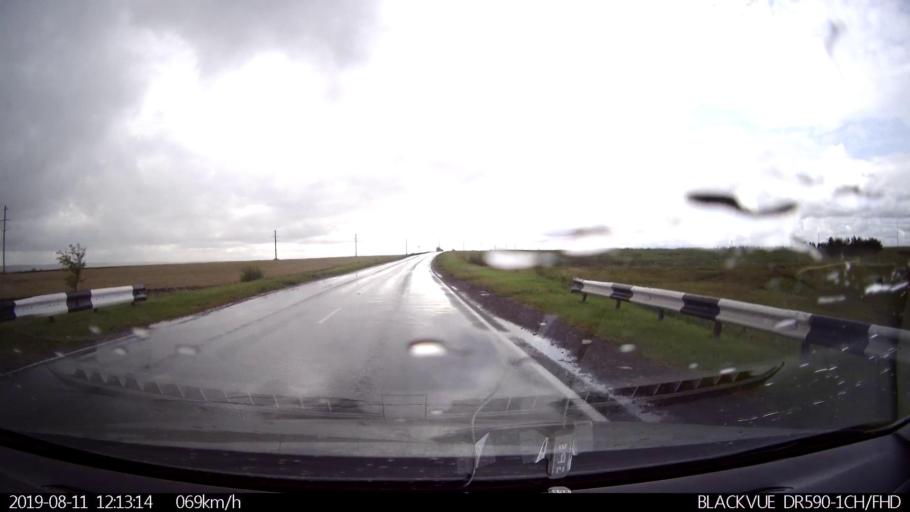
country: RU
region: Ulyanovsk
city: Silikatnyy
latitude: 53.9640
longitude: 47.9934
